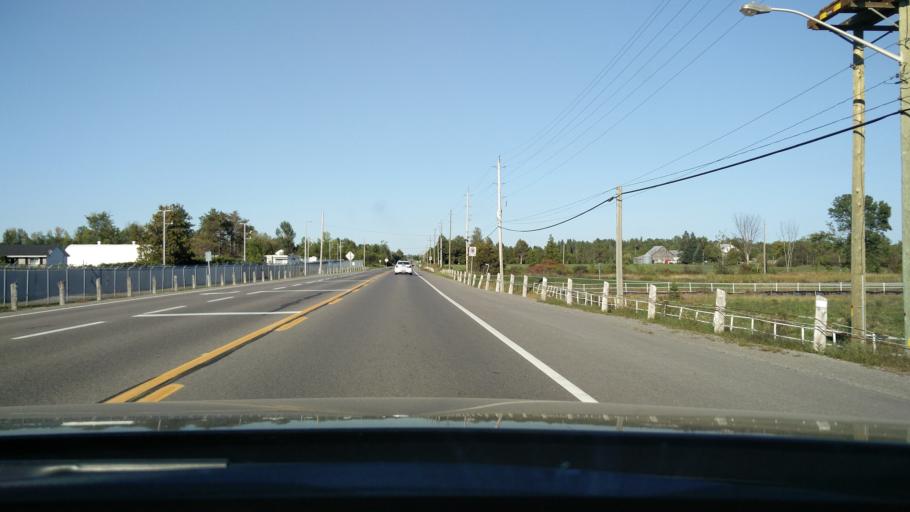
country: CA
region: Ontario
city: Carleton Place
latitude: 45.1279
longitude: -75.9445
